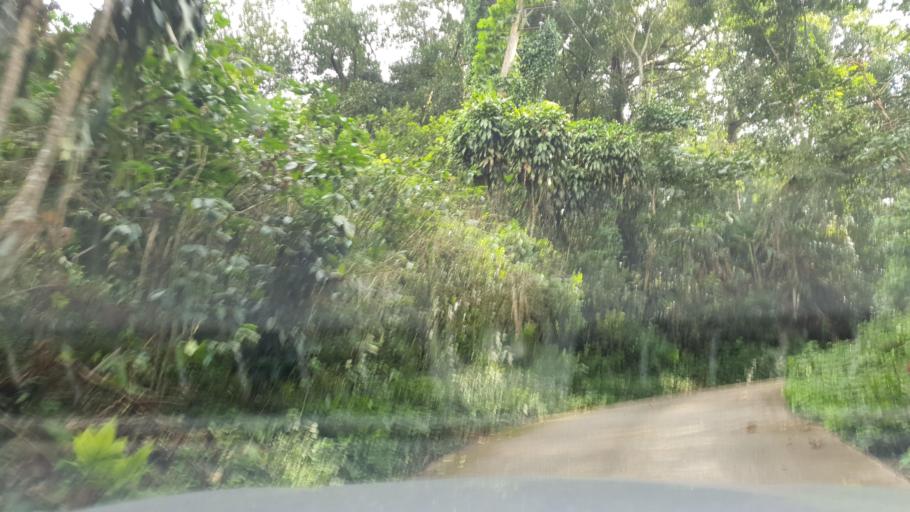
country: TH
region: Chiang Mai
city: Mae On
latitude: 18.9521
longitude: 99.3087
